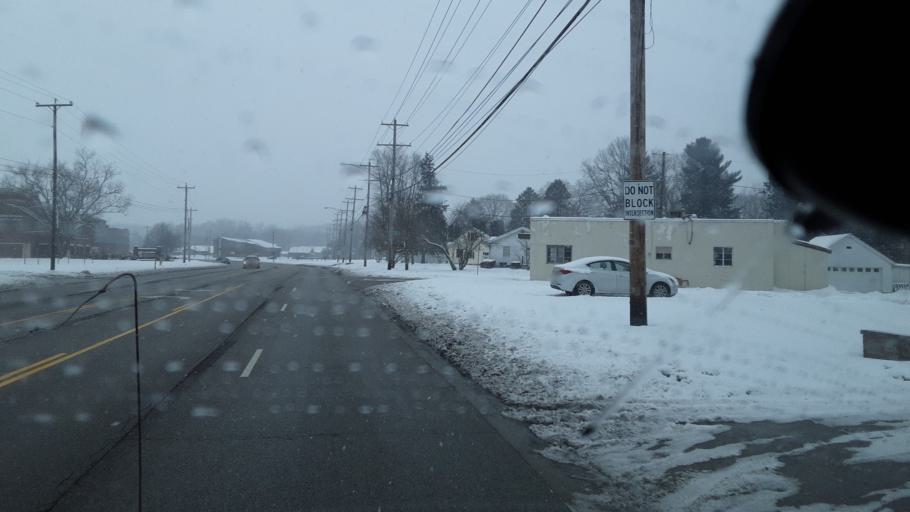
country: US
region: Ohio
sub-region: Licking County
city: Heath
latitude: 40.0441
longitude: -82.4624
